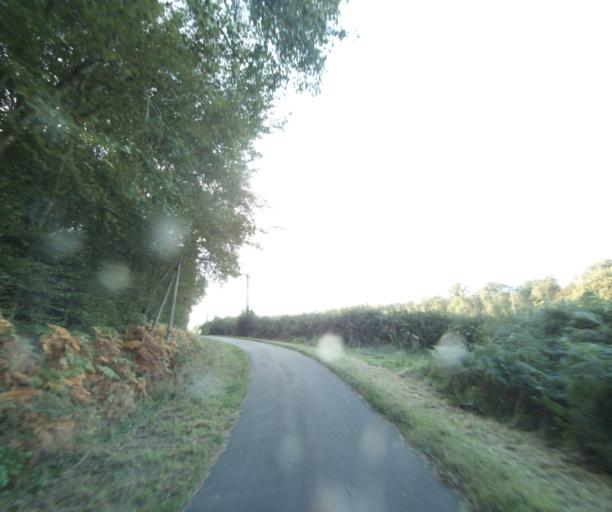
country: FR
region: Bourgogne
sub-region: Departement de Saone-et-Loire
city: Perrecy-les-Forges
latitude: 46.5938
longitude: 4.1823
